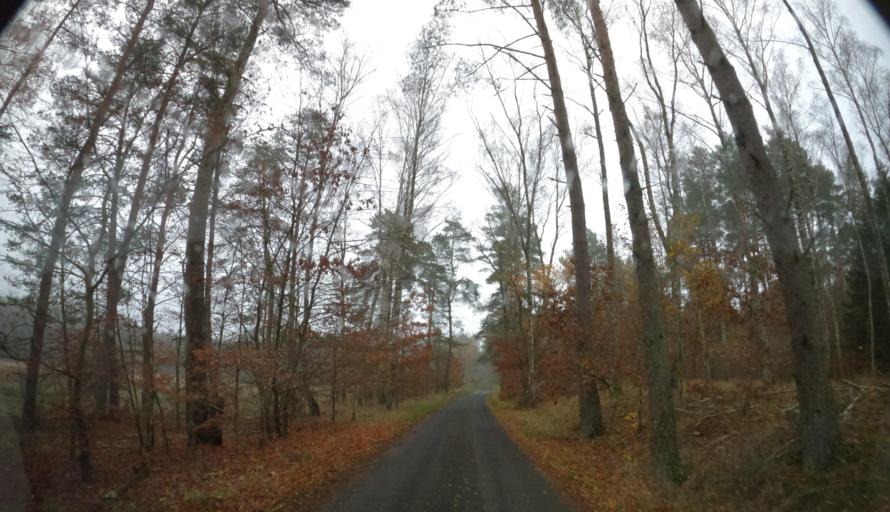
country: PL
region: West Pomeranian Voivodeship
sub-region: Powiat lobeski
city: Radowo Male
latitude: 53.6687
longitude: 15.4828
